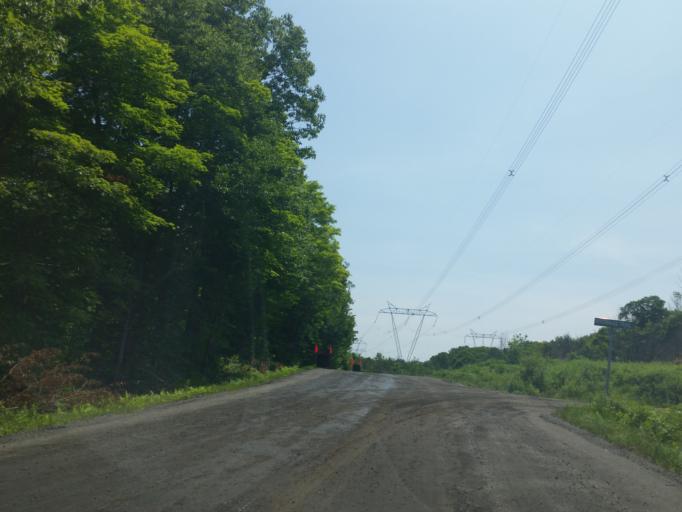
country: CA
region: Ontario
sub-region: Parry Sound District
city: Parry Sound
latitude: 45.4321
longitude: -80.0144
